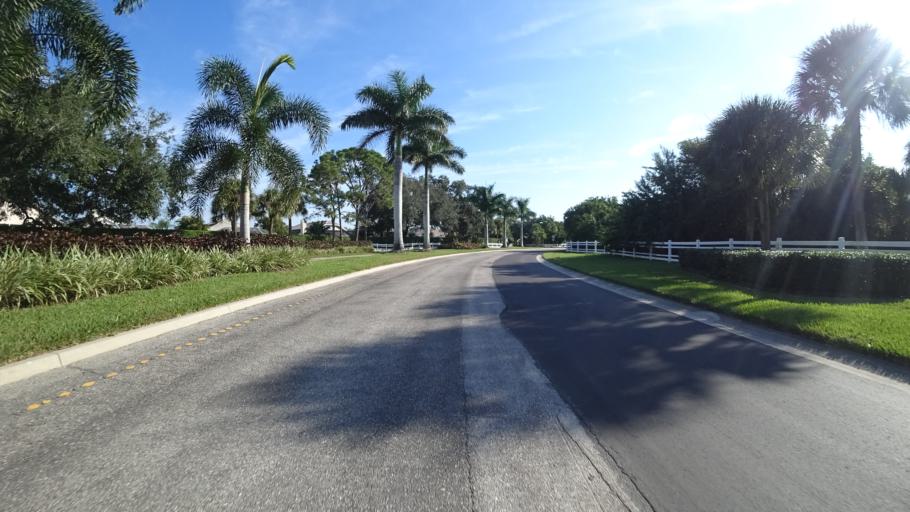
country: US
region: Florida
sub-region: Sarasota County
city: Desoto Lakes
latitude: 27.4173
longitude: -82.4836
